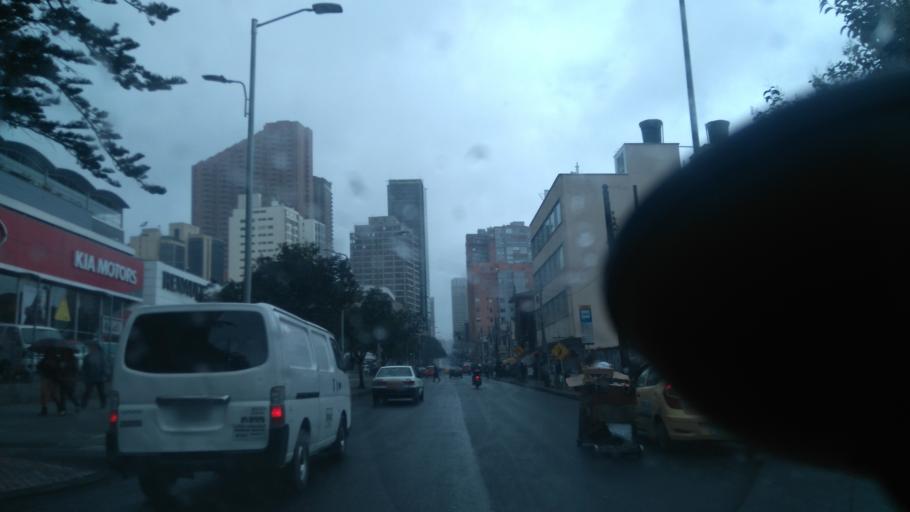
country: CO
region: Bogota D.C.
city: Bogota
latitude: 4.6230
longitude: -74.0680
